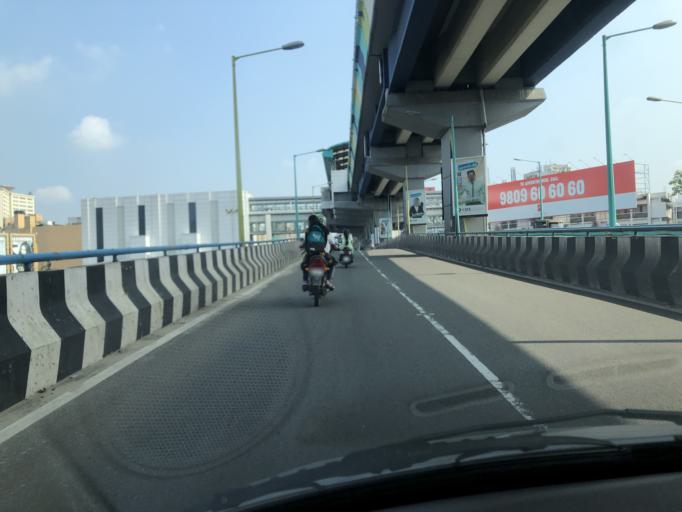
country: IN
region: Kerala
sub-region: Ernakulam
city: Elur
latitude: 10.0238
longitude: 76.3075
